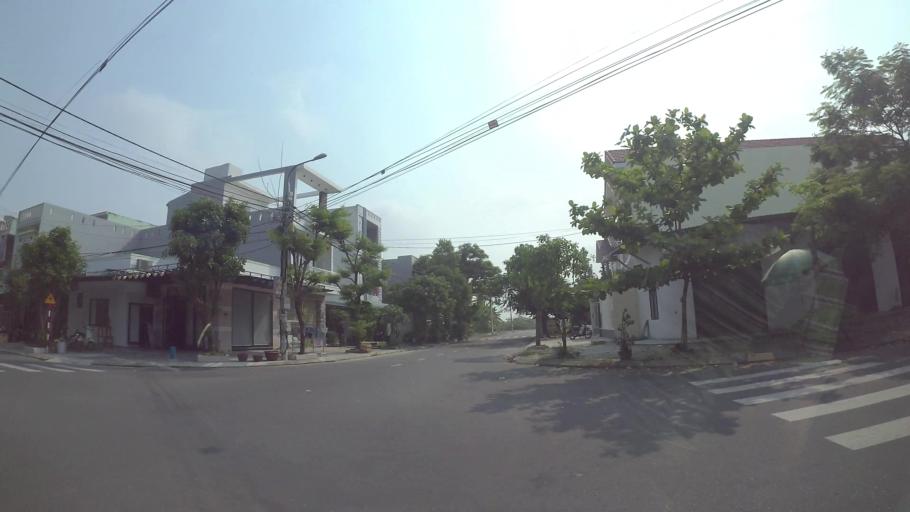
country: VN
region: Da Nang
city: Cam Le
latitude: 15.9926
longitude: 108.2152
